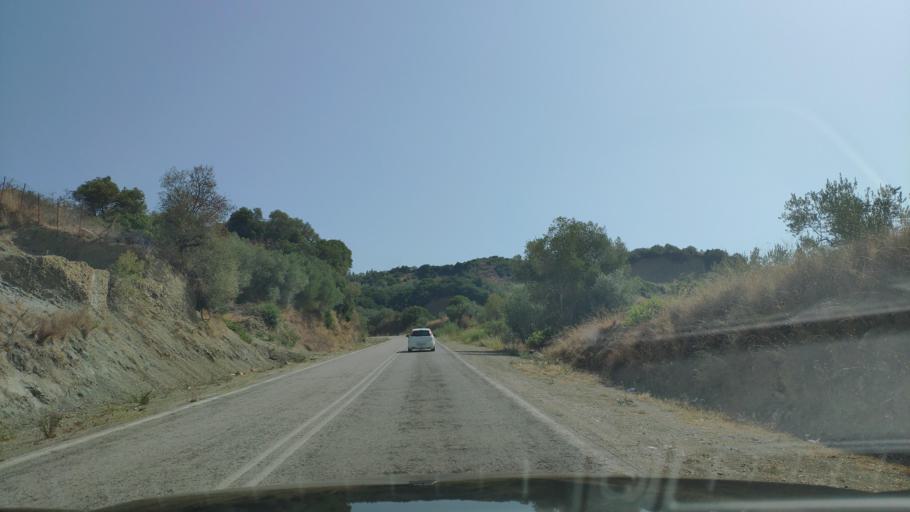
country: GR
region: Epirus
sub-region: Nomos Artas
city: Peta
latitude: 39.1672
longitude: 21.0393
